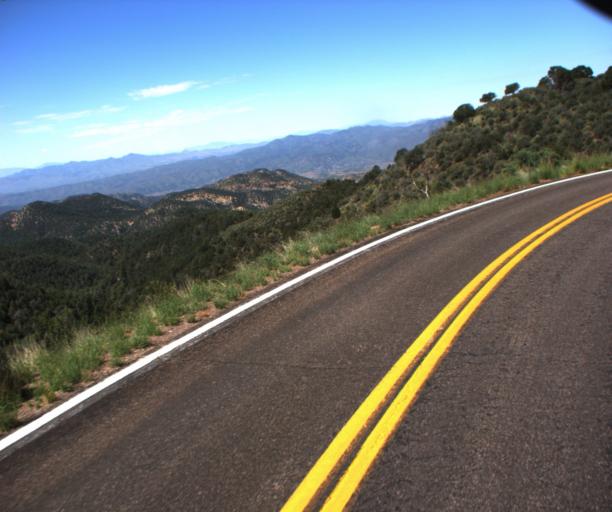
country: US
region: Arizona
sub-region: Greenlee County
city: Morenci
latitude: 33.2168
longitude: -109.3809
